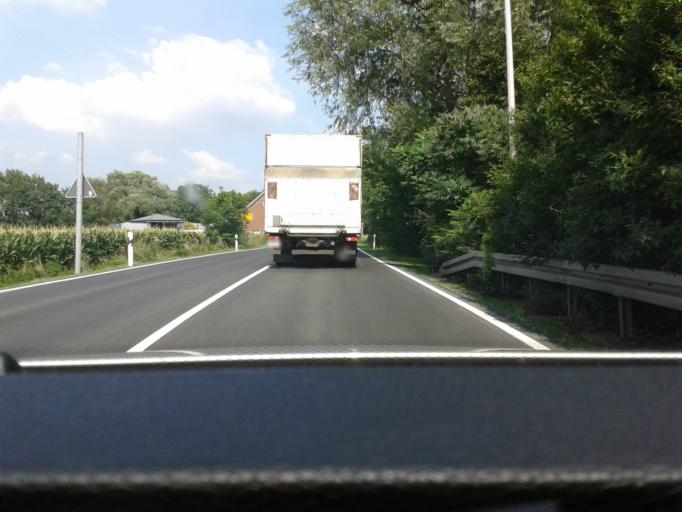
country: DE
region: North Rhine-Westphalia
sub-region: Regierungsbezirk Dusseldorf
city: Hochfeld
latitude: 51.4254
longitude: 6.6995
